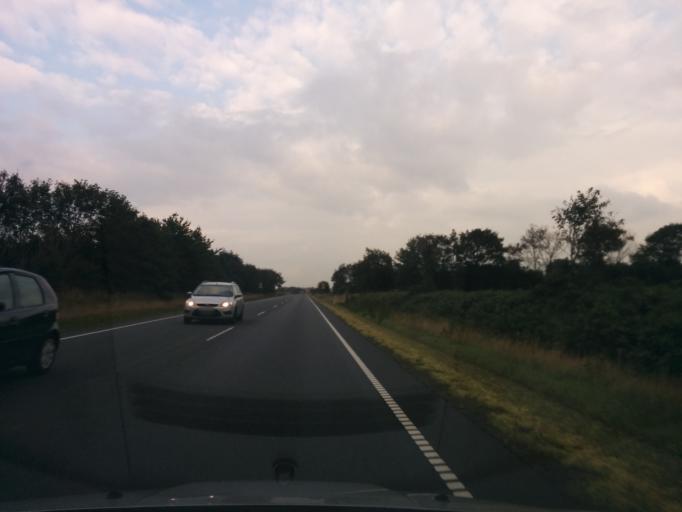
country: DK
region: South Denmark
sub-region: Esbjerg Kommune
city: Bramming
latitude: 55.5978
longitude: 8.7236
